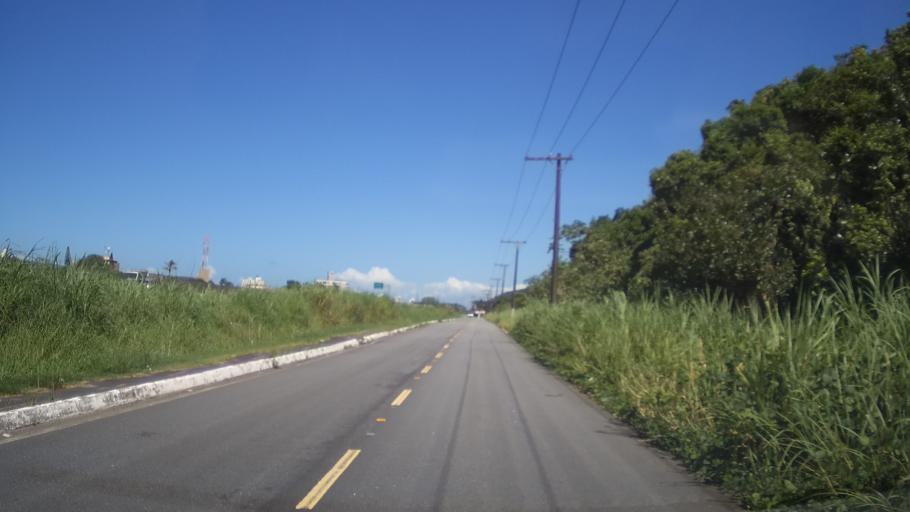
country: BR
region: Sao Paulo
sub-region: Mongagua
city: Mongagua
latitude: -24.0741
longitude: -46.5861
